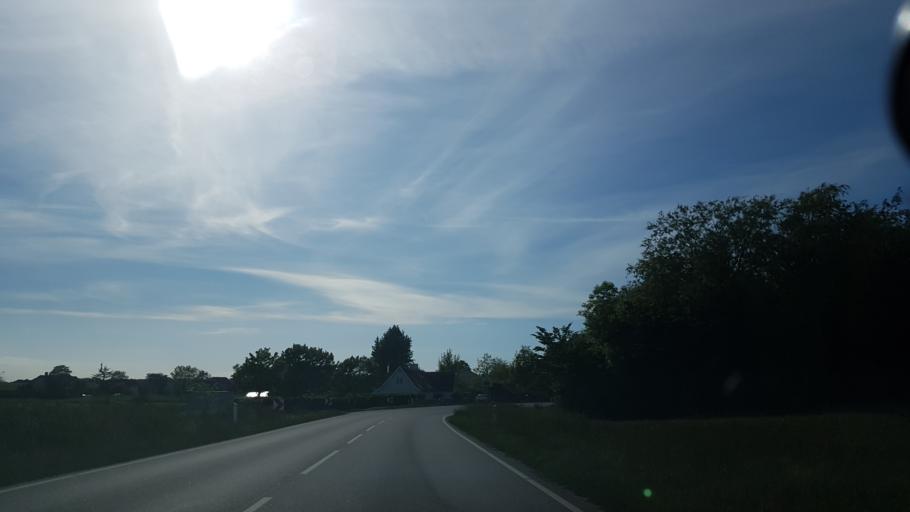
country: DK
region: Zealand
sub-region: Slagelse Kommune
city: Forlev
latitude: 55.4328
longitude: 11.2791
